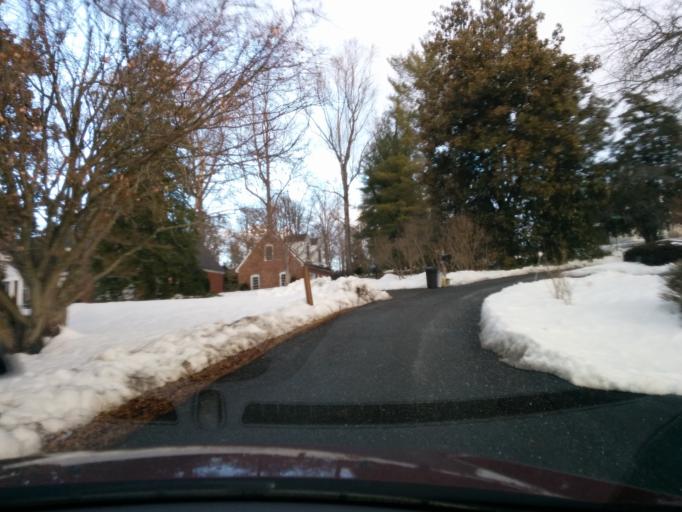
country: US
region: Virginia
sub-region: City of Lexington
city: Lexington
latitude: 37.7825
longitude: -79.4544
